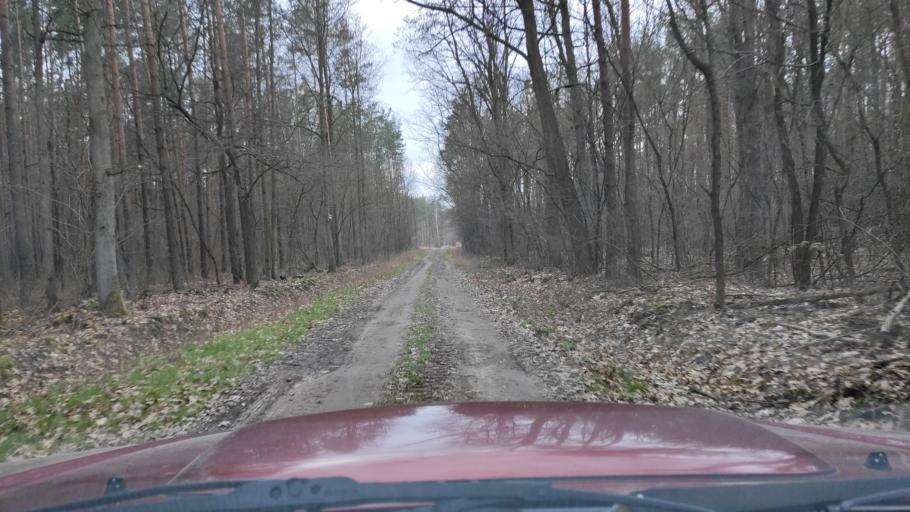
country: PL
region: Masovian Voivodeship
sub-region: Powiat kozienicki
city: Garbatka-Letnisko
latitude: 51.5101
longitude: 21.5459
